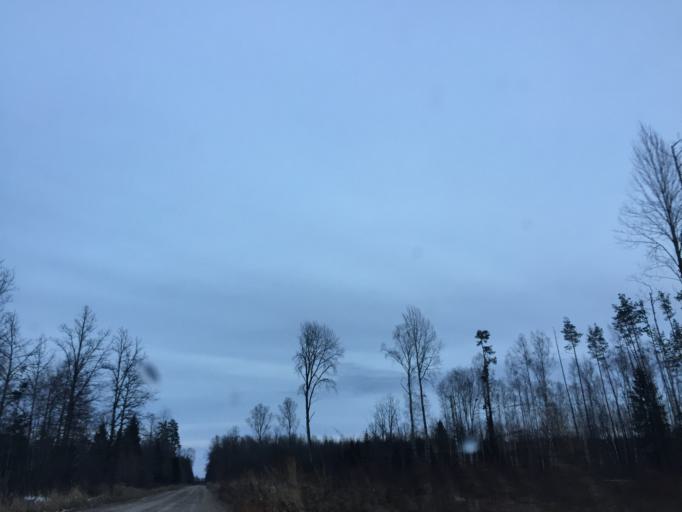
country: LV
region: Burtnieki
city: Matisi
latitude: 57.6301
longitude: 25.1461
